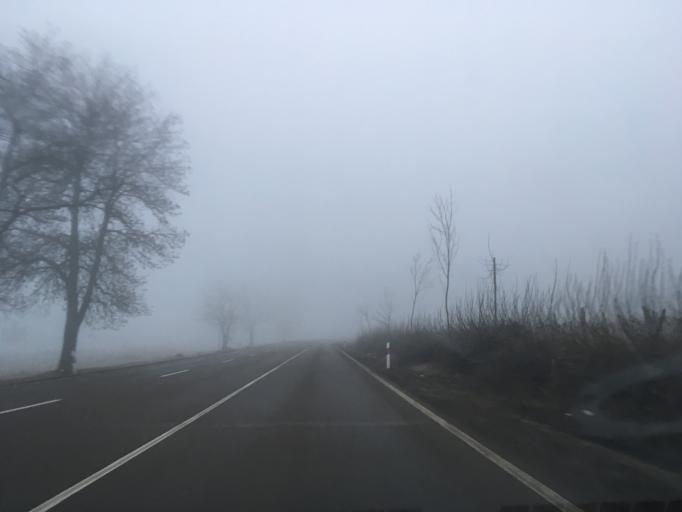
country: HU
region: Heves
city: Kerecsend
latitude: 47.8104
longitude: 20.3581
